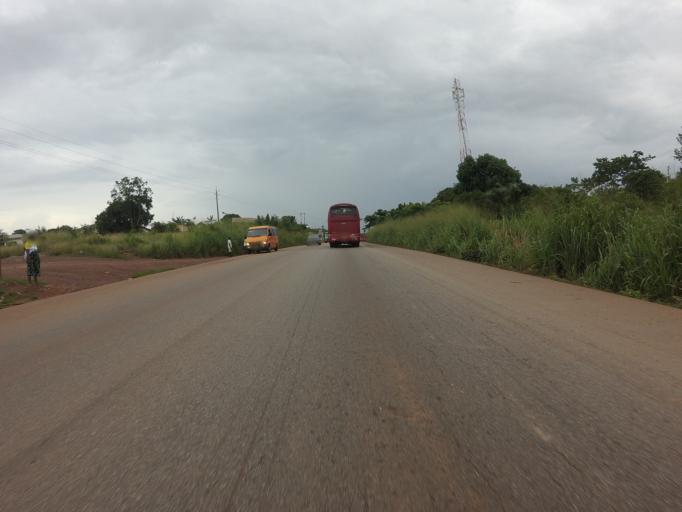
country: GH
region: Ashanti
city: Konongo
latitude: 6.6176
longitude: -1.1876
